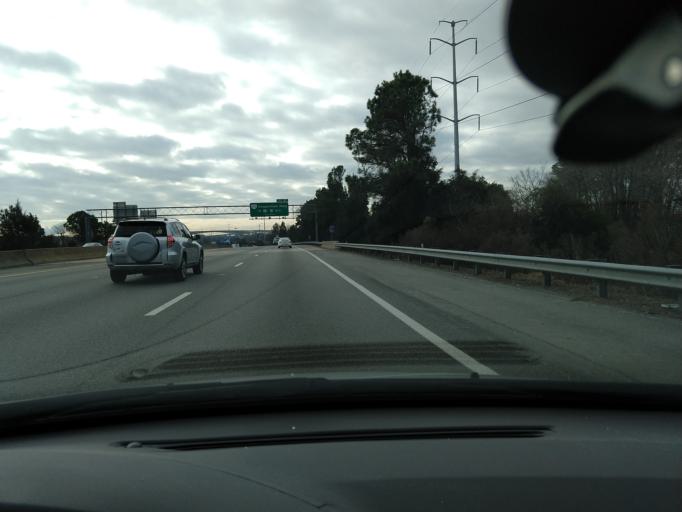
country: US
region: Virginia
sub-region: Chesterfield County
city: Bensley
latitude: 37.4580
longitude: -77.4256
